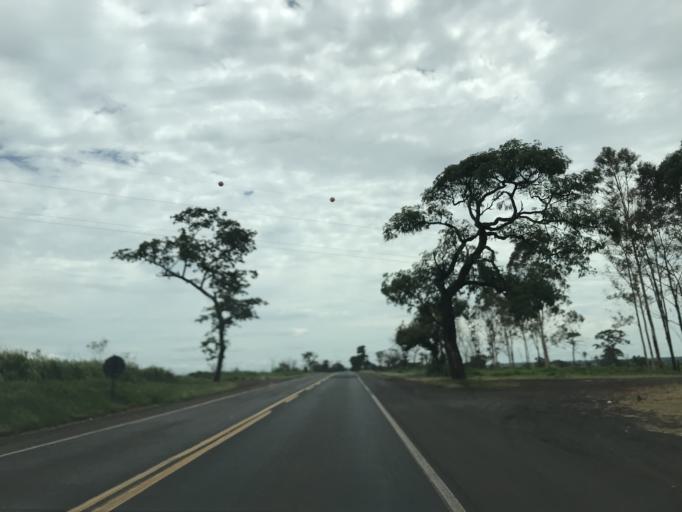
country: BR
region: Minas Gerais
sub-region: Frutal
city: Frutal
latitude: -19.9996
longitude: -49.0402
